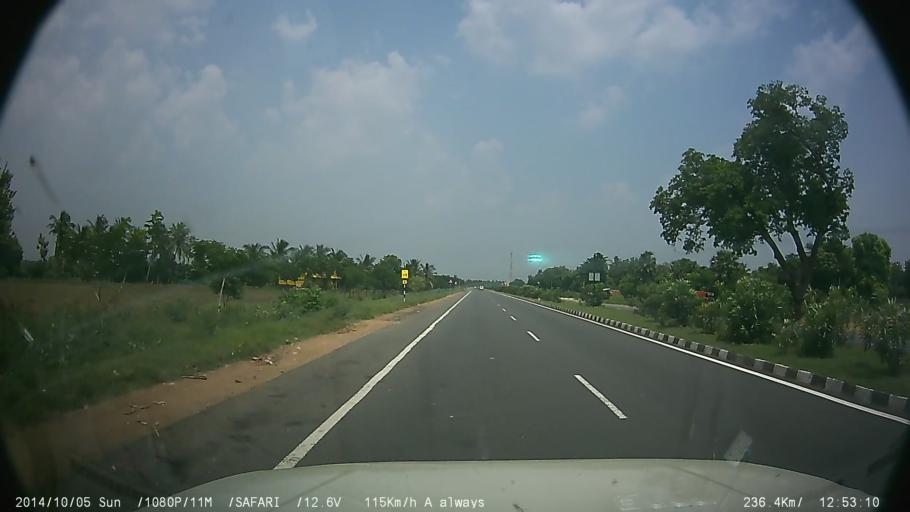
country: IN
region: Tamil Nadu
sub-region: Cuddalore
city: Panruti
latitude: 11.7442
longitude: 79.3648
